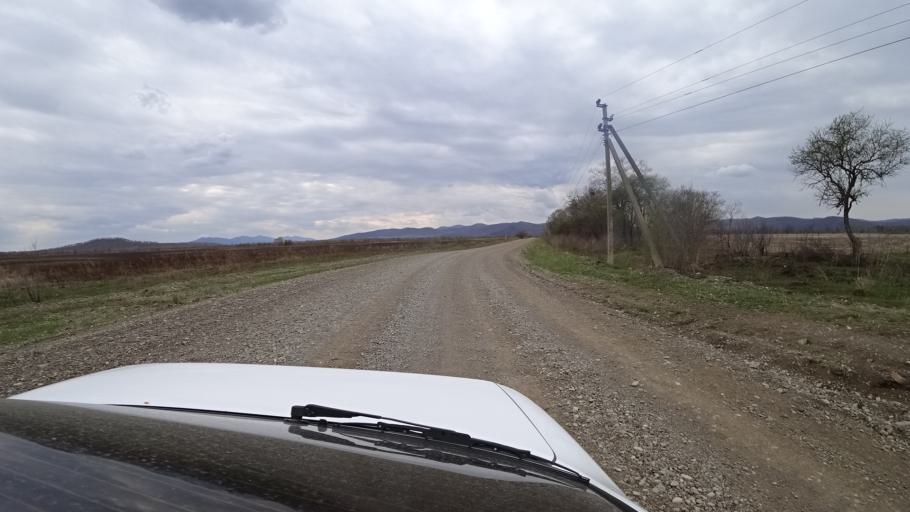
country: RU
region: Primorskiy
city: Novopokrovka
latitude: 45.5769
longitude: 134.3101
